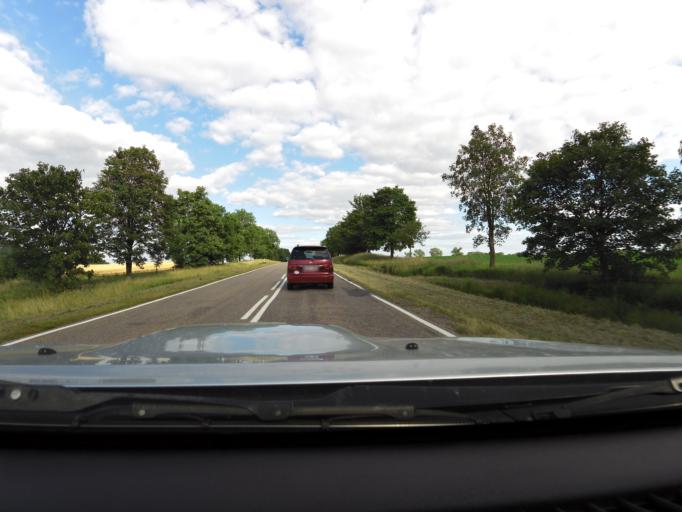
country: PL
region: Podlasie
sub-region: Powiat grajewski
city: Rajgrod
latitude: 53.8610
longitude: 22.7174
